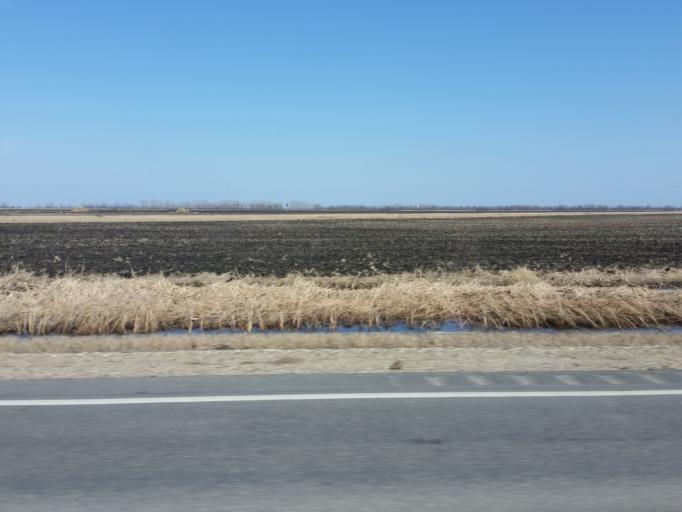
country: US
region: North Dakota
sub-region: Grand Forks County
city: Grand Forks Air Force Base
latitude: 48.1349
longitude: -97.2493
